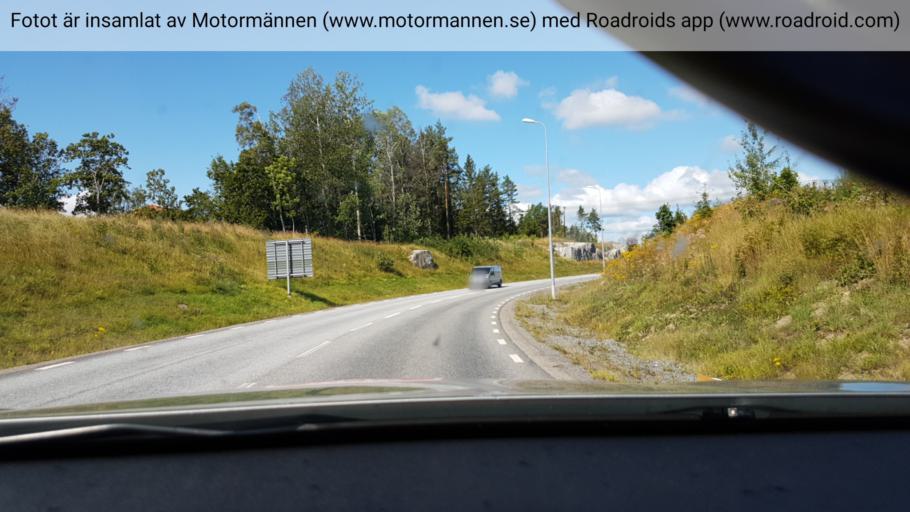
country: SE
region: Stockholm
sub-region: Norrtalje Kommun
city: Norrtalje
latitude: 59.7658
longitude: 18.6919
